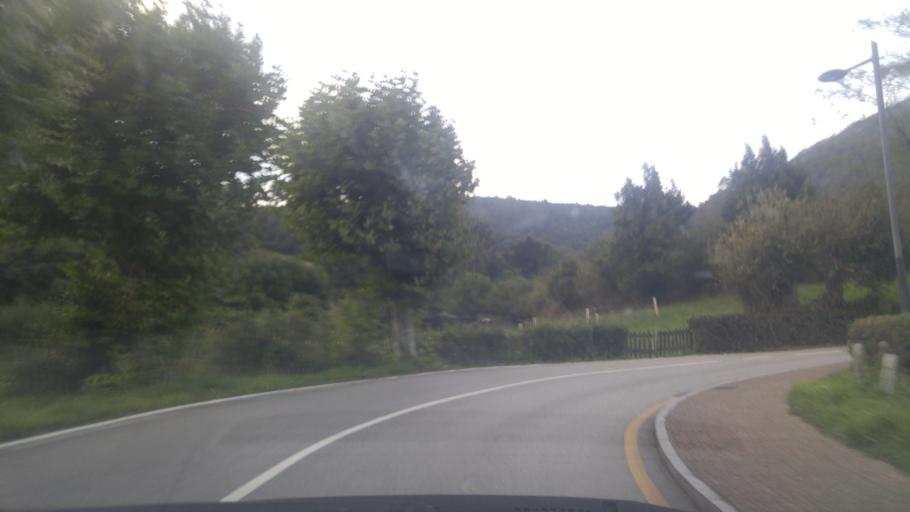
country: ES
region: Asturias
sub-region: Province of Asturias
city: Oviedo
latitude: 43.3772
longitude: -5.8666
